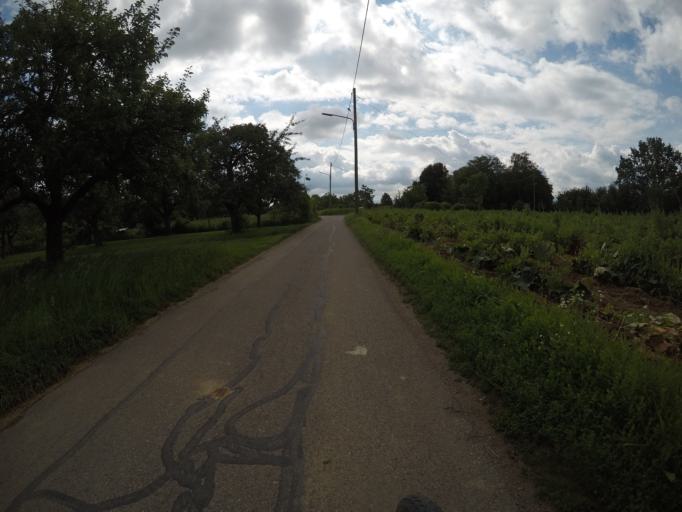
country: DE
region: Baden-Wuerttemberg
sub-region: Regierungsbezirk Stuttgart
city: Esslingen
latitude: 48.7233
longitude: 9.2867
